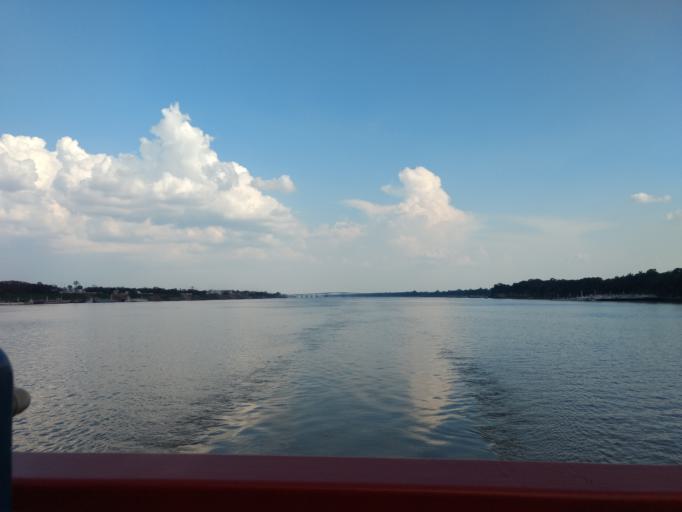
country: BR
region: Rondonia
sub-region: Porto Velho
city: Porto Velho
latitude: -8.6931
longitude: -63.9219
